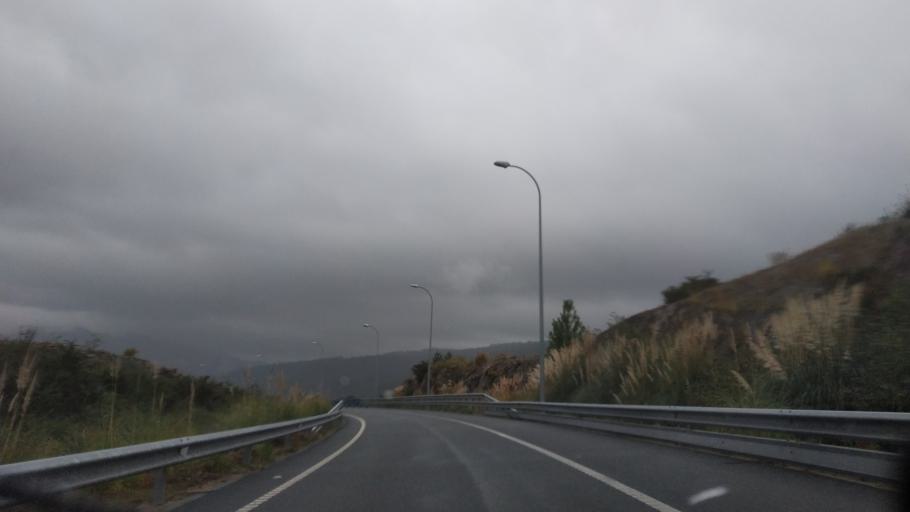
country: ES
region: Galicia
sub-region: Provincia da Coruna
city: Culleredo
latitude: 43.2760
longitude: -8.4006
